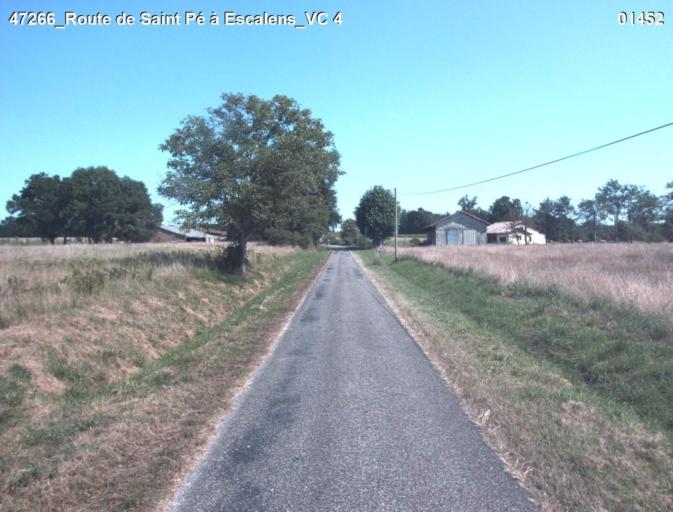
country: FR
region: Aquitaine
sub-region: Departement des Landes
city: Gabarret
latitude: 44.0005
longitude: 0.0778
